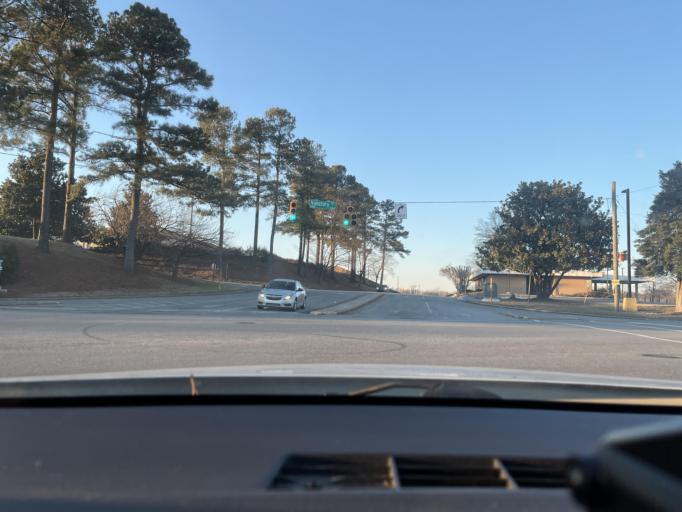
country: US
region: North Carolina
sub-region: Guilford County
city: Greensboro
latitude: 36.0381
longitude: -79.8350
